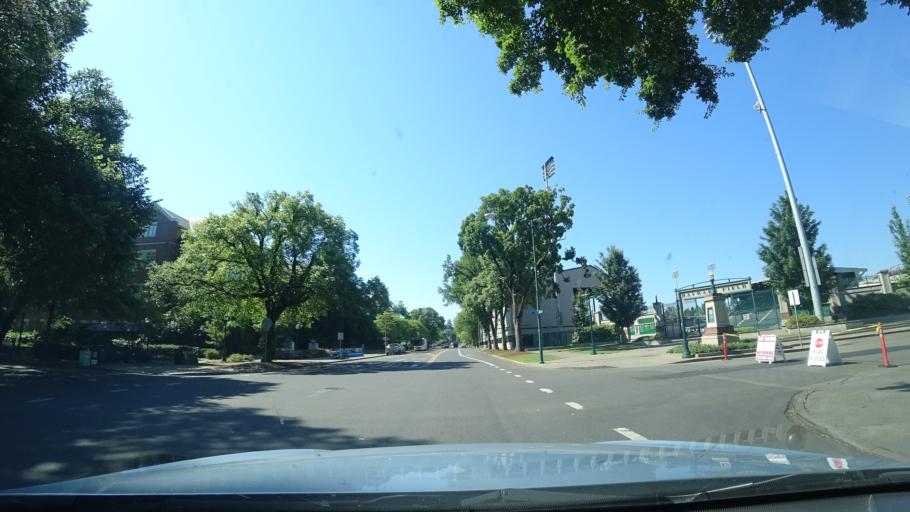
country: US
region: Oregon
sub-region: Lane County
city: Eugene
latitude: 44.0436
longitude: -123.0697
